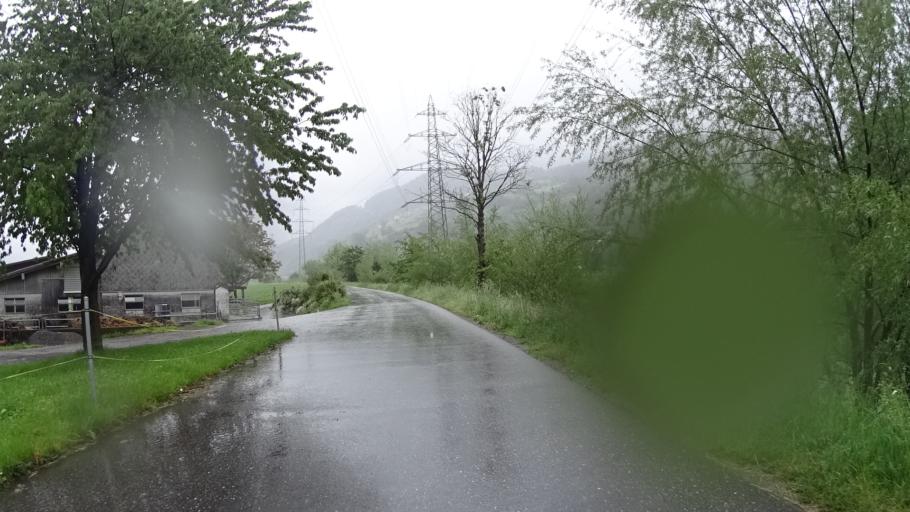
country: CH
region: Saint Gallen
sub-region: Wahlkreis Sarganserland
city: Flums
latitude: 47.0886
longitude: 9.3543
